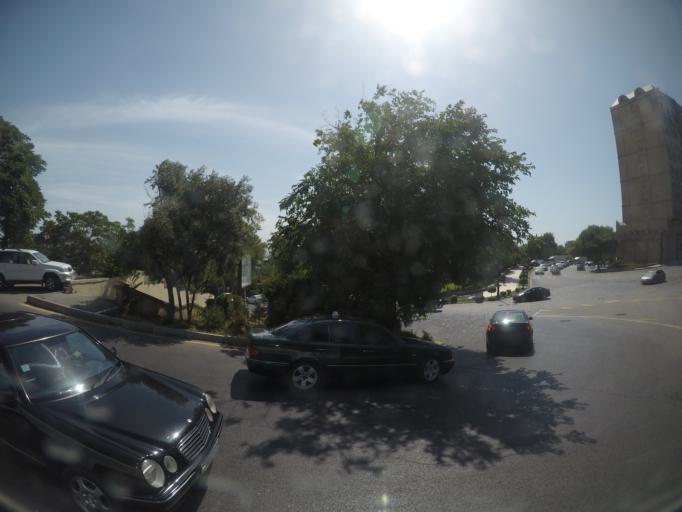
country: AZ
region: Baki
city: Badamdar
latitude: 40.3640
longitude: 49.8262
